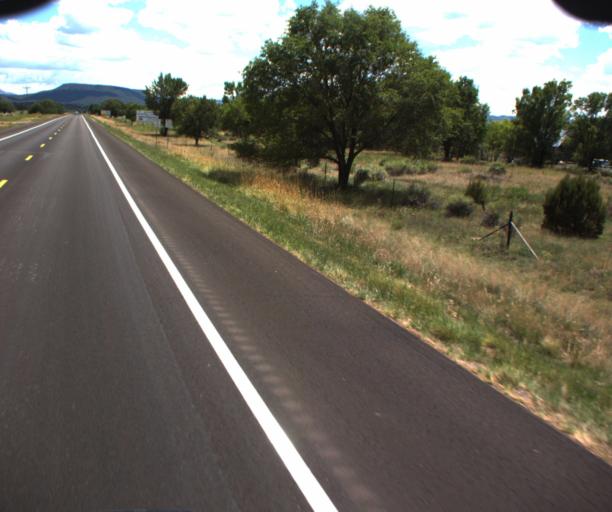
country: US
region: Arizona
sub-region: Apache County
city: Springerville
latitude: 34.1561
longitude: -109.3004
